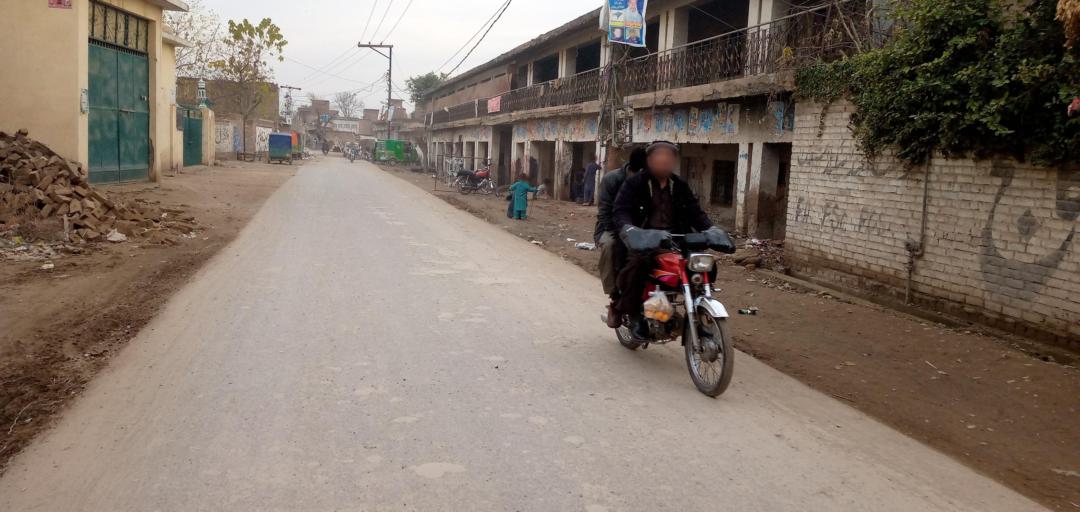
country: PK
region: Khyber Pakhtunkhwa
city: Peshawar
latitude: 34.0203
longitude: 71.4953
